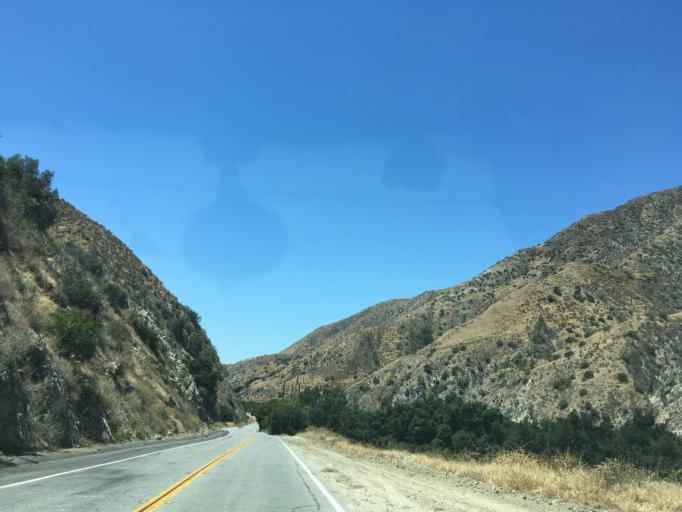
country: US
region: California
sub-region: Los Angeles County
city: La Crescenta-Montrose
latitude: 34.2989
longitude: -118.2786
